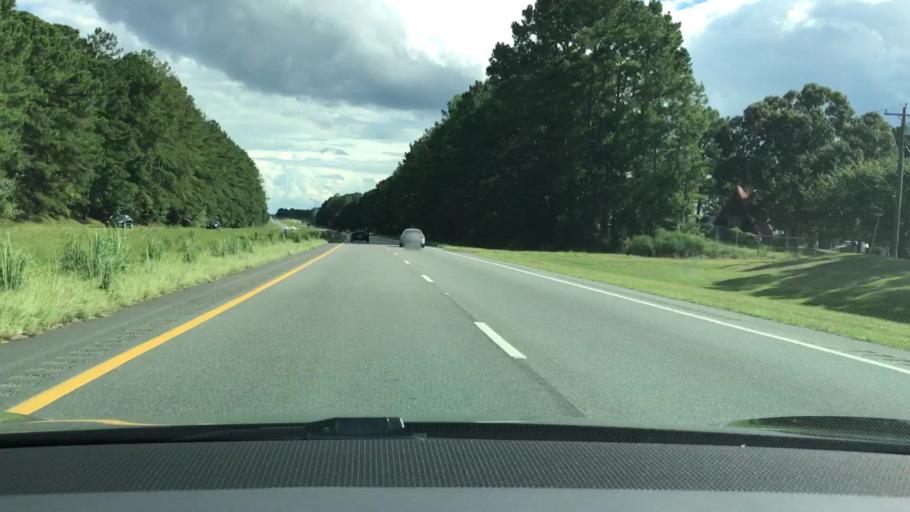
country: US
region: Alabama
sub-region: Pike County
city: Troy
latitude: 31.8949
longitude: -86.0100
